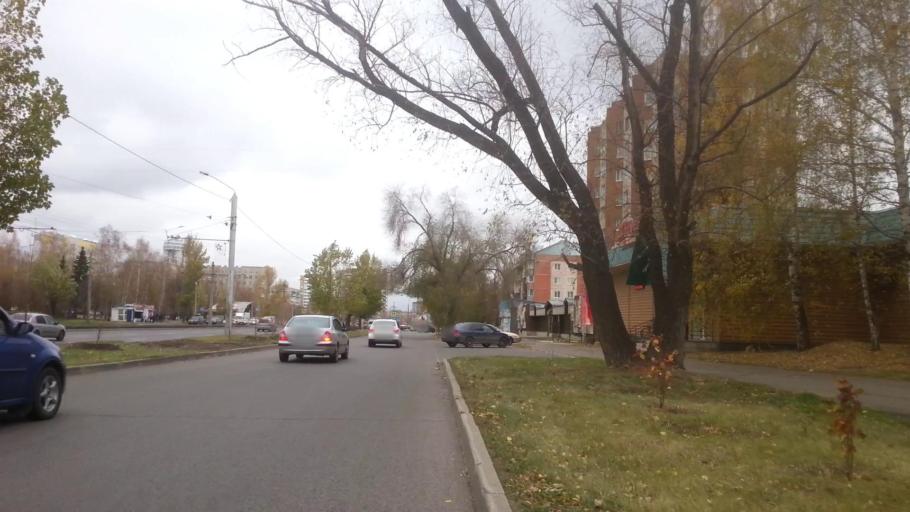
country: RU
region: Altai Krai
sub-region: Gorod Barnaulskiy
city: Barnaul
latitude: 53.3651
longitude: 83.7057
